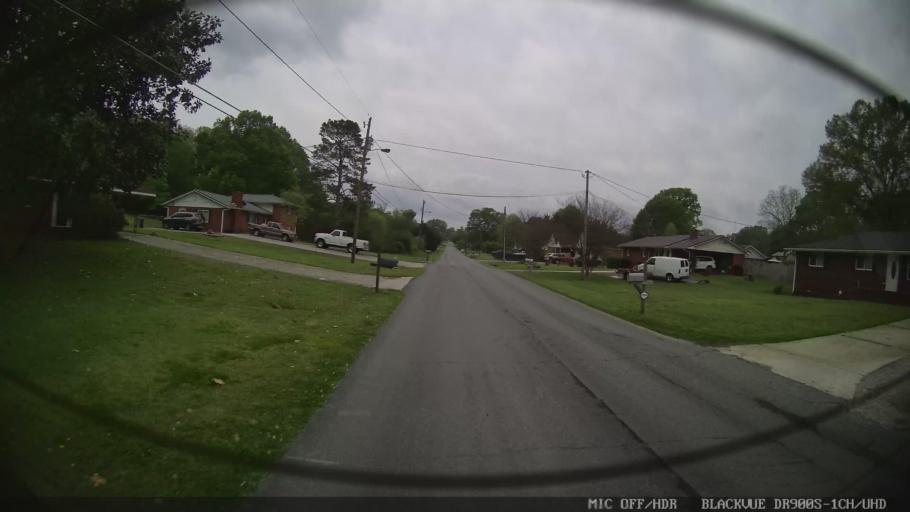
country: US
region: Georgia
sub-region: Bartow County
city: Cartersville
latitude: 34.2023
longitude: -84.8168
